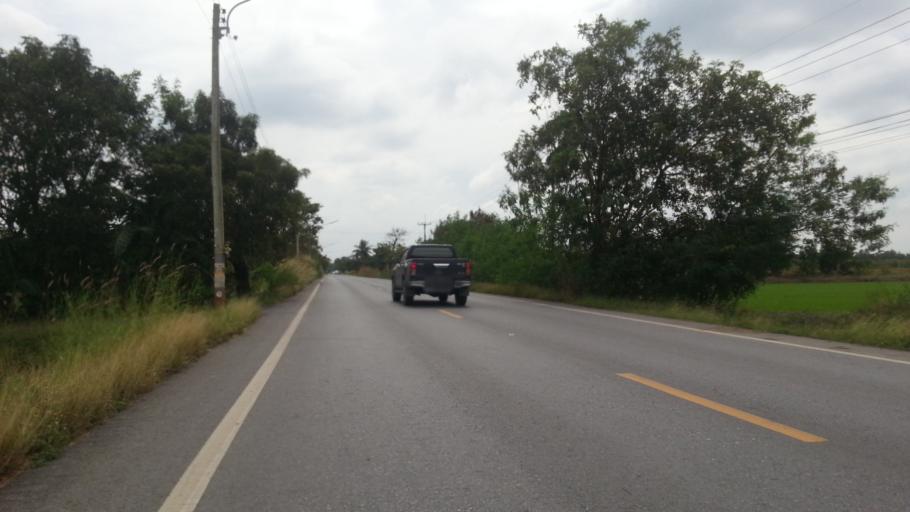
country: TH
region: Pathum Thani
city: Ban Lam Luk Ka
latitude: 14.0261
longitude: 100.8437
